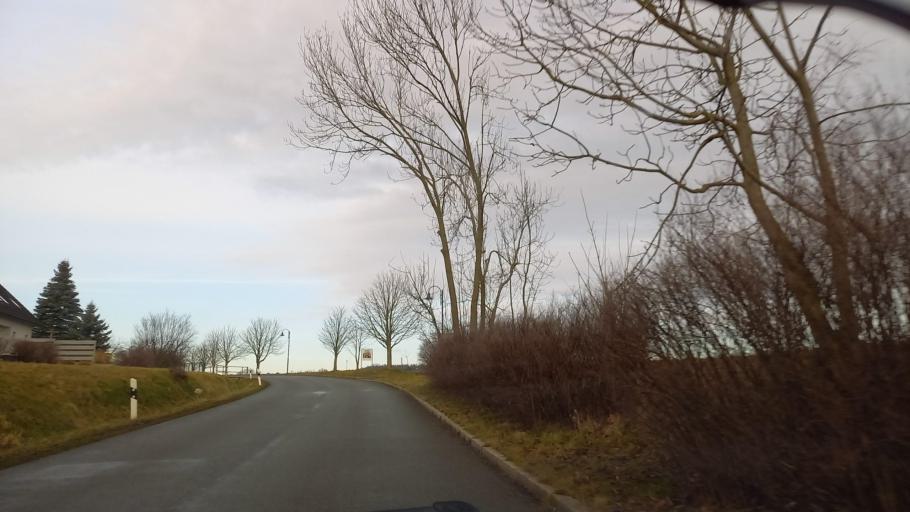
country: DE
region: Saxony
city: Hirschfeld
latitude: 50.6253
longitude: 12.4525
